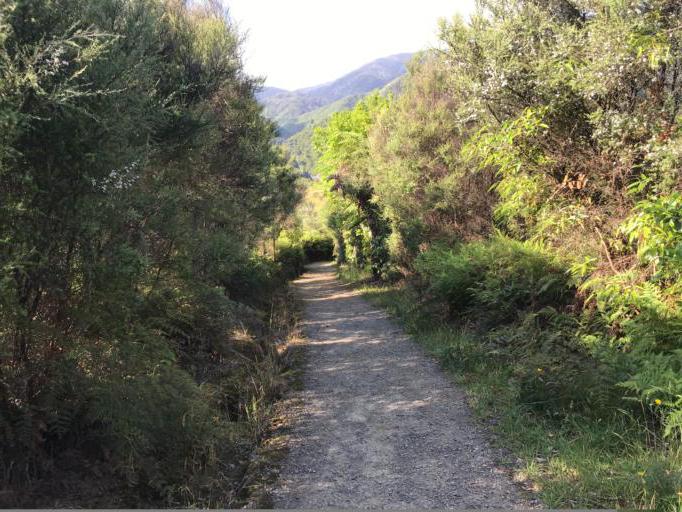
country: NZ
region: Wellington
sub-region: Kapiti Coast District
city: Otaki
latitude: -40.8761
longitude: 175.2346
